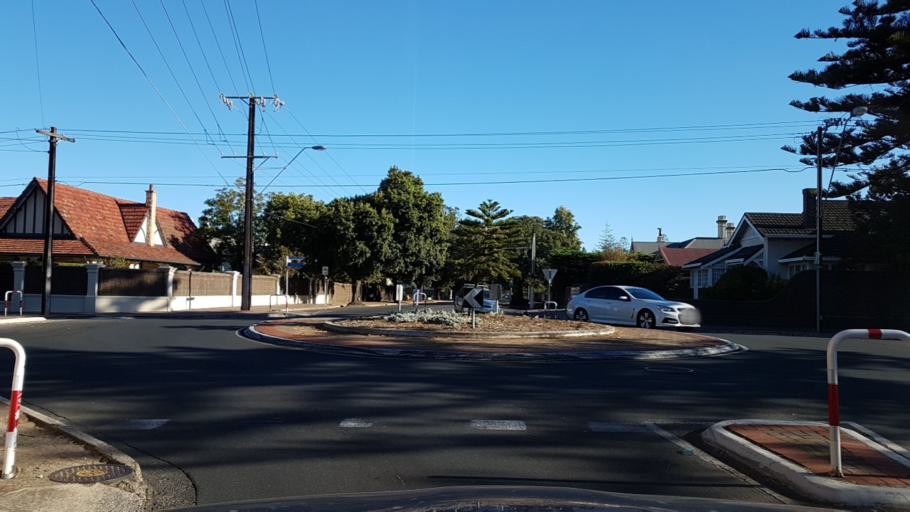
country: AU
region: South Australia
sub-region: Adelaide
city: Glenelg
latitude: -34.9884
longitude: 138.5138
